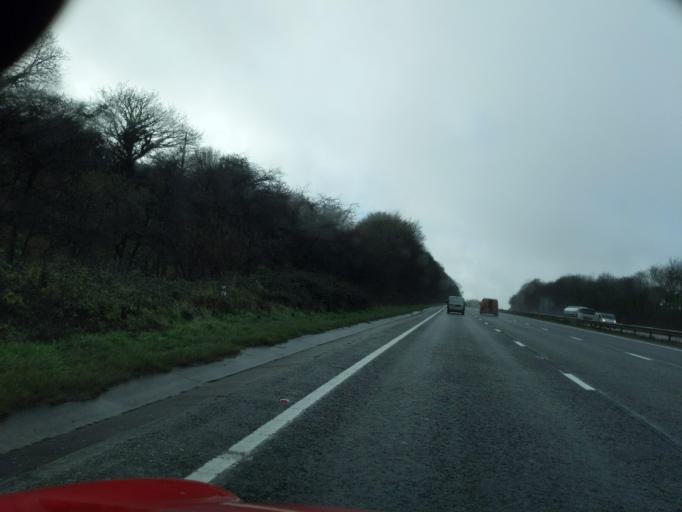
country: GB
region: England
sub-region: Devon
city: Plympton
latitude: 50.3781
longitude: -4.0270
